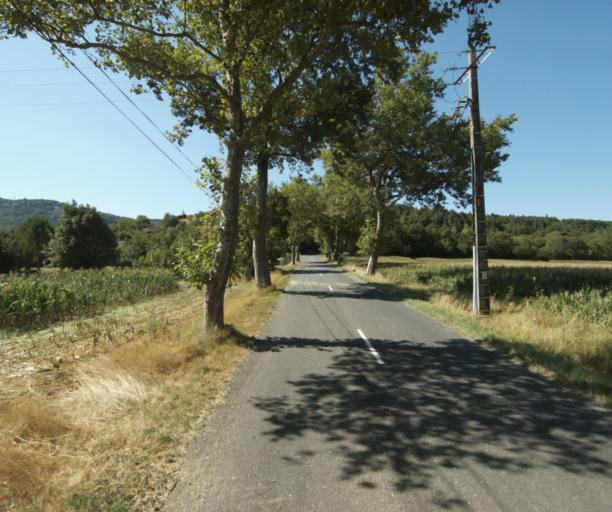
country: FR
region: Midi-Pyrenees
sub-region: Departement du Tarn
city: Soreze
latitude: 43.4491
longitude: 2.0457
